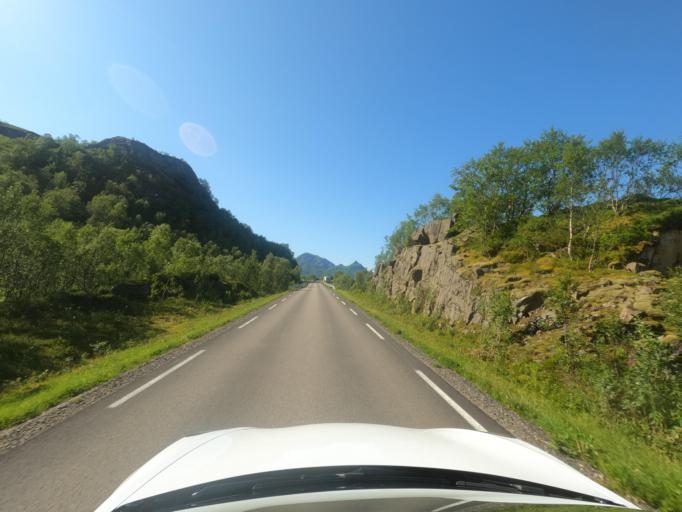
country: NO
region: Nordland
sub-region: Hadsel
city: Stokmarknes
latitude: 68.3274
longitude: 15.0121
